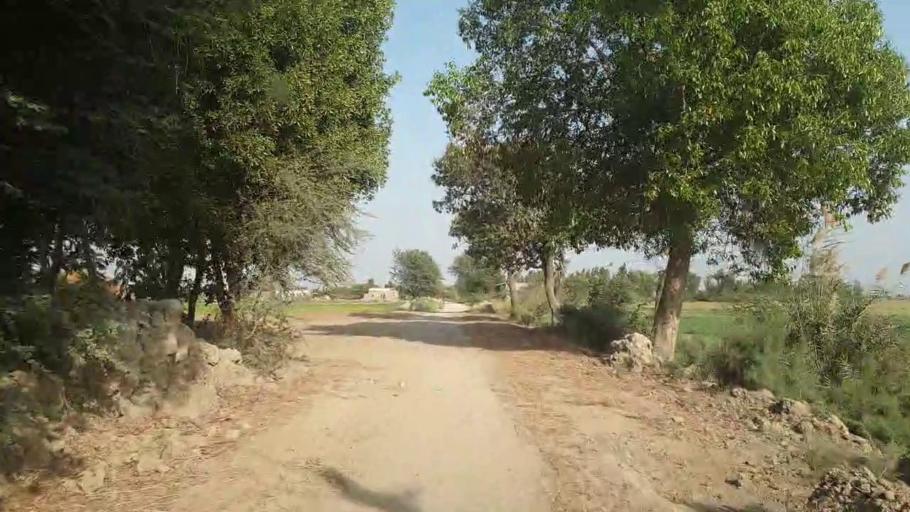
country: PK
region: Sindh
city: Kario
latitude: 24.5997
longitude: 68.5460
